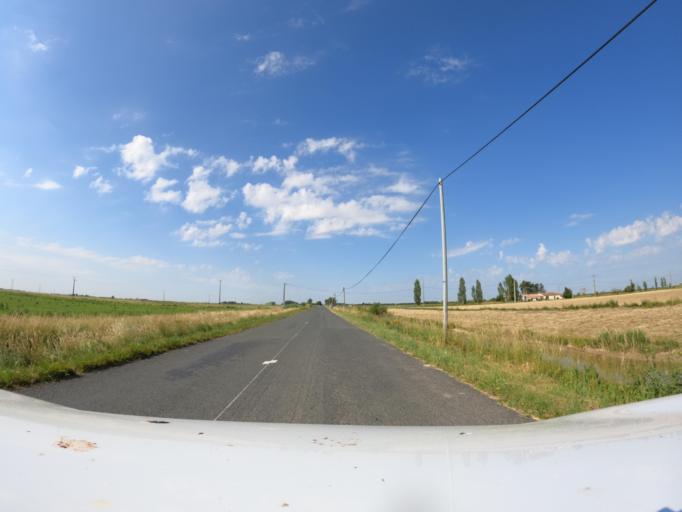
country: FR
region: Pays de la Loire
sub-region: Departement de la Vendee
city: Champagne-les-Marais
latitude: 46.3628
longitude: -1.1117
